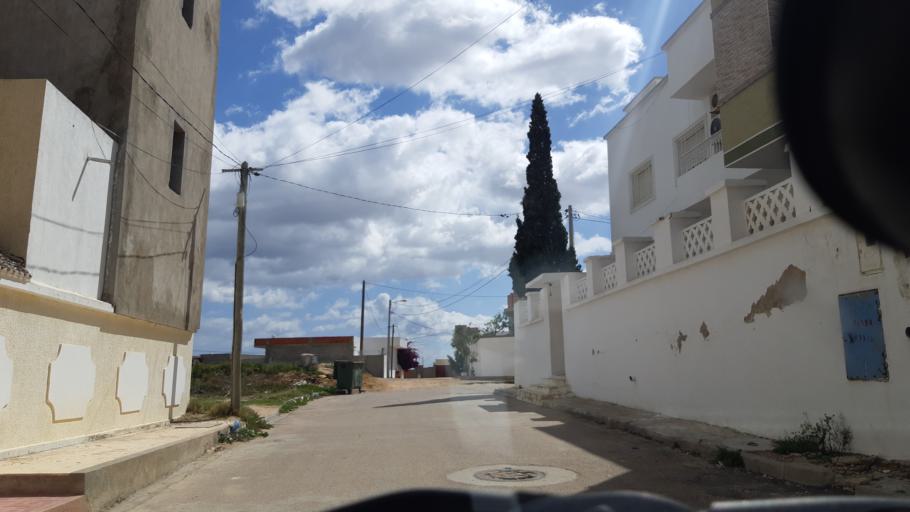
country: TN
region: Susah
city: Akouda
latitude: 35.8781
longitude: 10.5453
